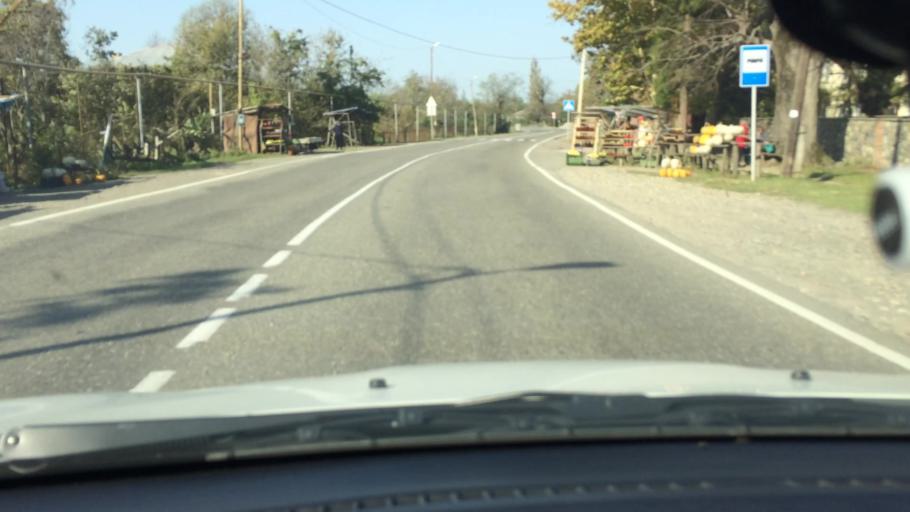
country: GE
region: Guria
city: Lanchkhuti
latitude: 42.0856
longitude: 42.1140
